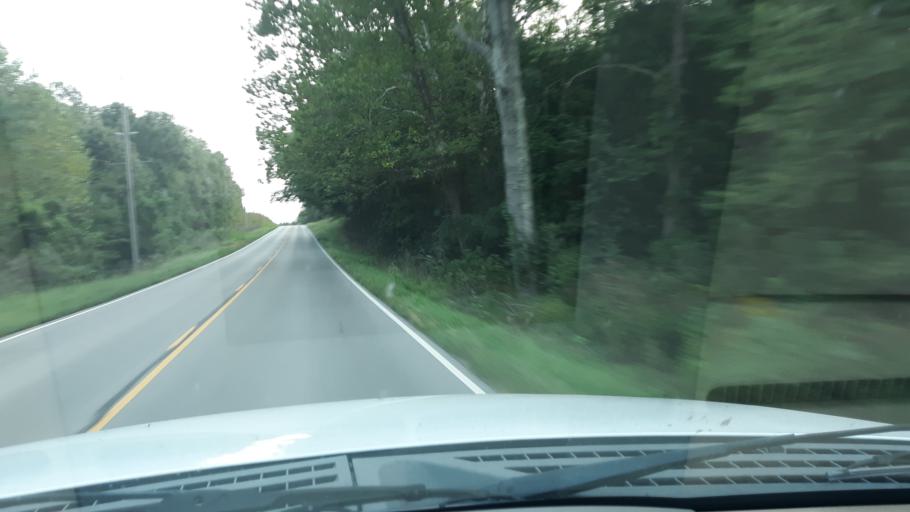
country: US
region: Illinois
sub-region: White County
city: Norris City
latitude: 37.9314
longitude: -88.3472
